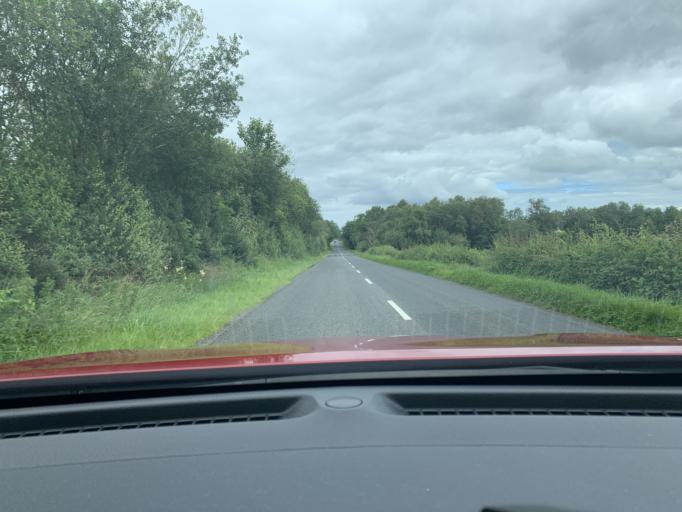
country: GB
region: Northern Ireland
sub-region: Fermanagh District
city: Enniskillen
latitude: 54.2863
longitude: -7.6992
